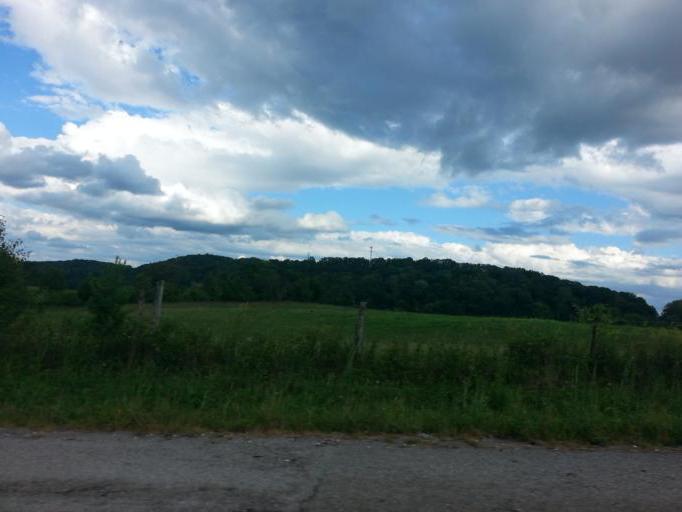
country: US
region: Tennessee
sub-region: Knox County
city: Knoxville
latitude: 36.0437
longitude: -83.8772
